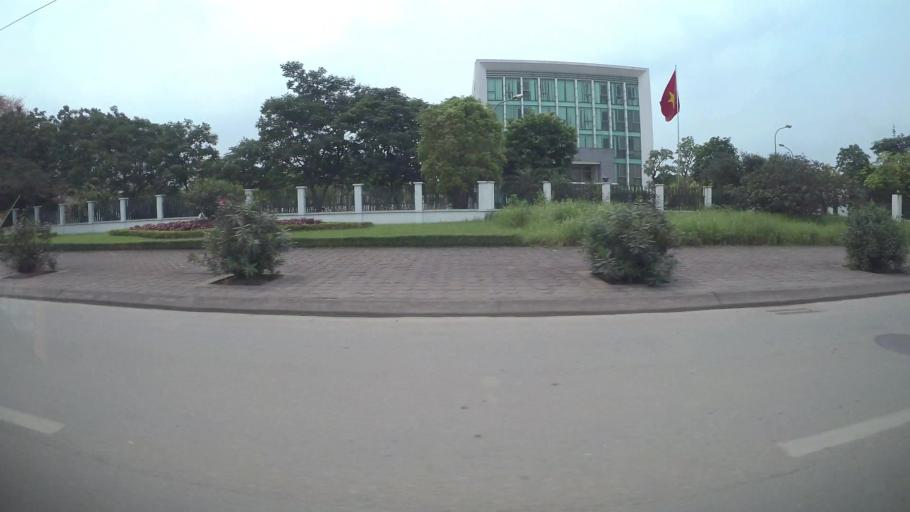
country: VN
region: Ha Noi
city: Trau Quy
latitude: 21.0628
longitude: 105.9030
